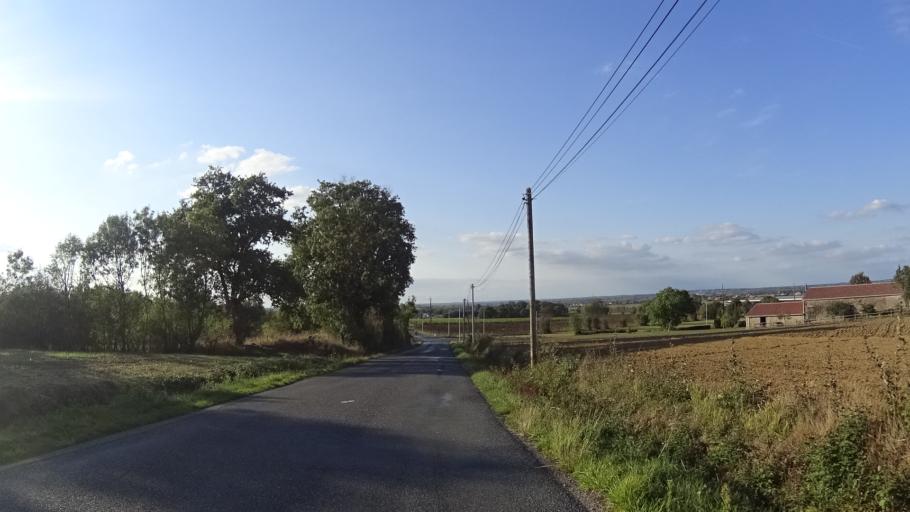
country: FR
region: Pays de la Loire
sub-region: Departement de Maine-et-Loire
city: La Chapelle-Saint-Florent
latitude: 47.3408
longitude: -1.0718
